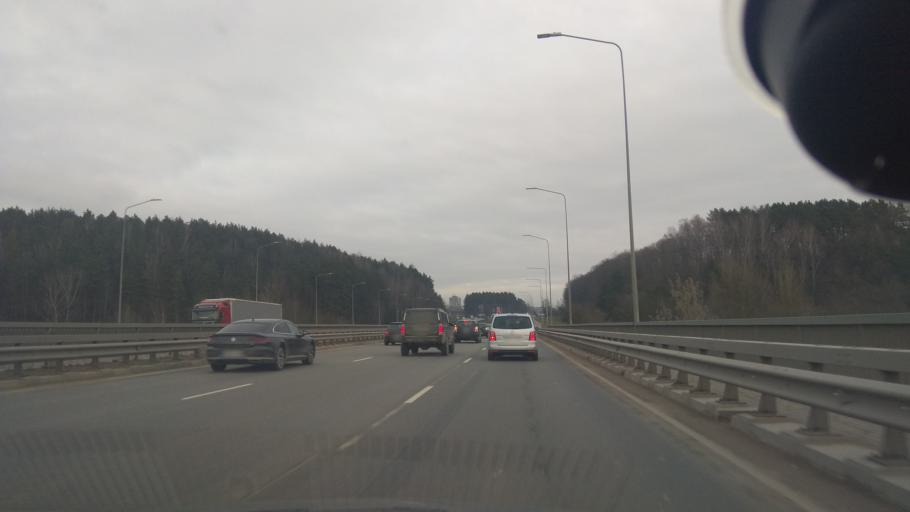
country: LT
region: Vilnius County
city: Lazdynai
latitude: 54.6696
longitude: 25.1832
